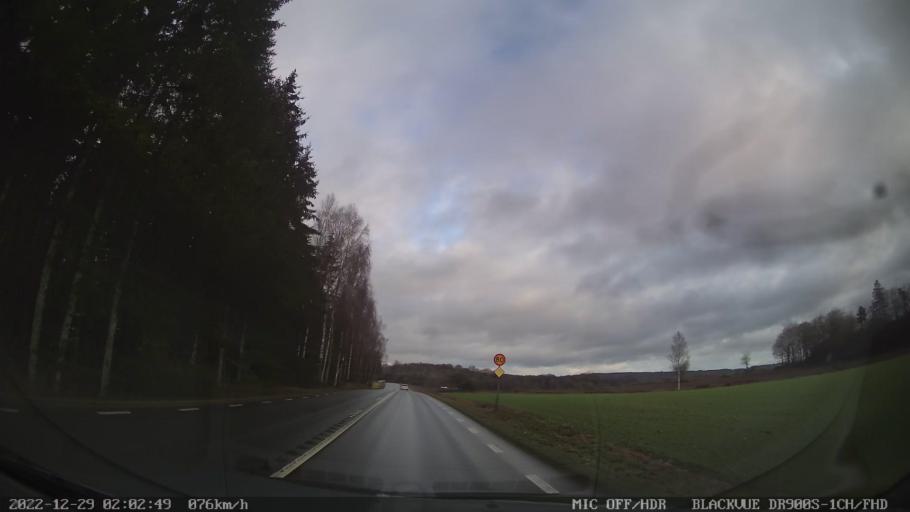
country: SE
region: Skane
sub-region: Simrishamns Kommun
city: Kivik
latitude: 55.6269
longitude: 14.1352
